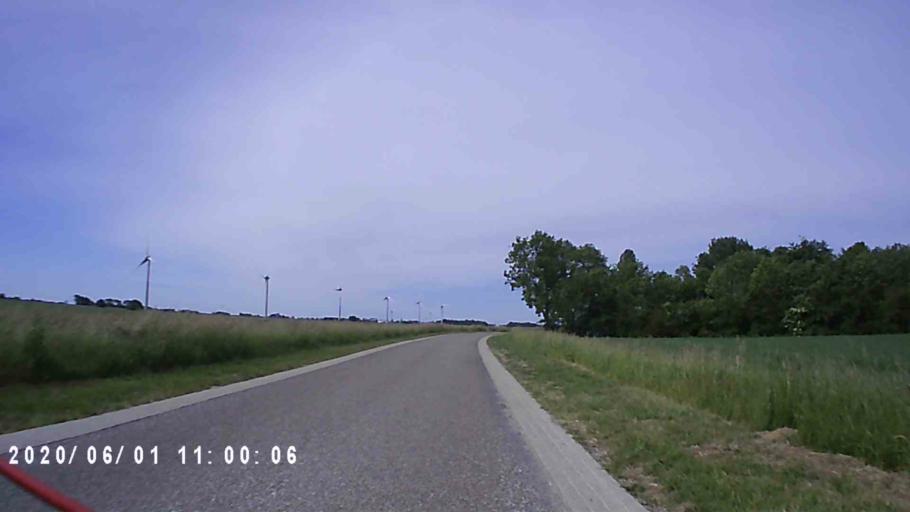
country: NL
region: Friesland
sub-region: Gemeente Franekeradeel
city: Sexbierum
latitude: 53.1974
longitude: 5.4885
